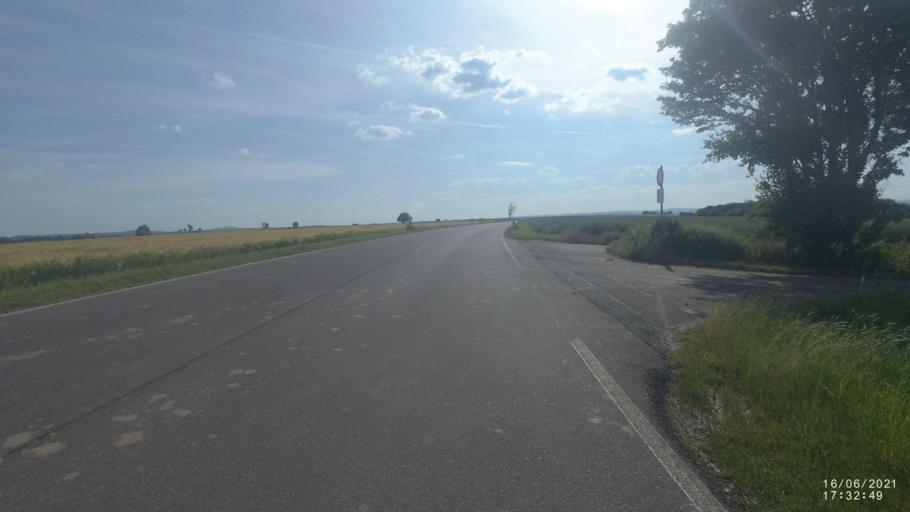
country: DE
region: Rheinland-Pfalz
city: Oberfell
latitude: 50.2724
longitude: 7.4259
